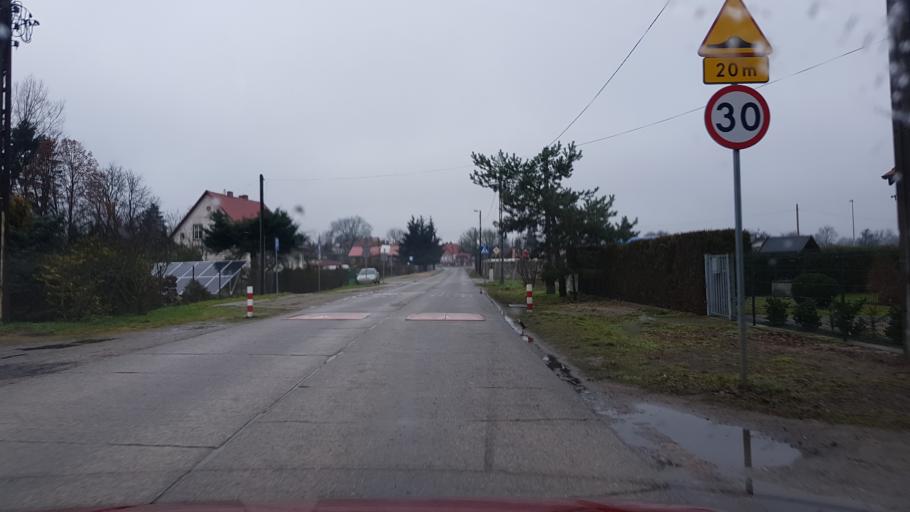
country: PL
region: West Pomeranian Voivodeship
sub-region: Powiat policki
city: Dobra
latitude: 53.5404
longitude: 14.4688
